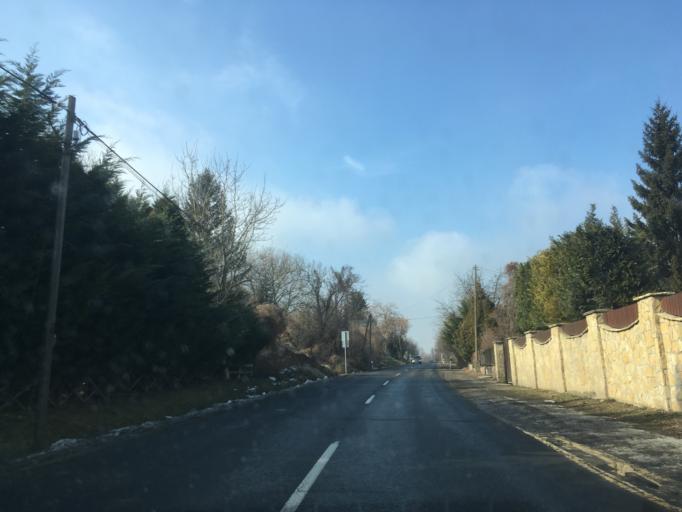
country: HU
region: Pest
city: Szob
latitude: 47.8136
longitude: 18.8111
